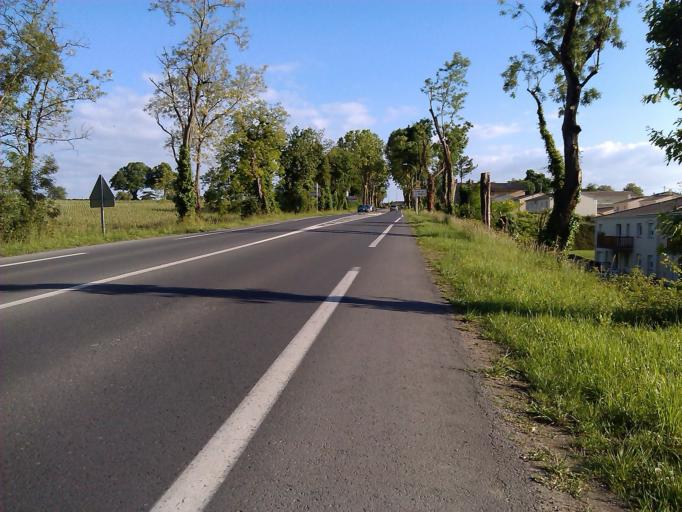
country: FR
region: Aquitaine
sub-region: Departement de la Gironde
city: Cubzac-les-Ponts
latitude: 44.9771
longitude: -0.4518
